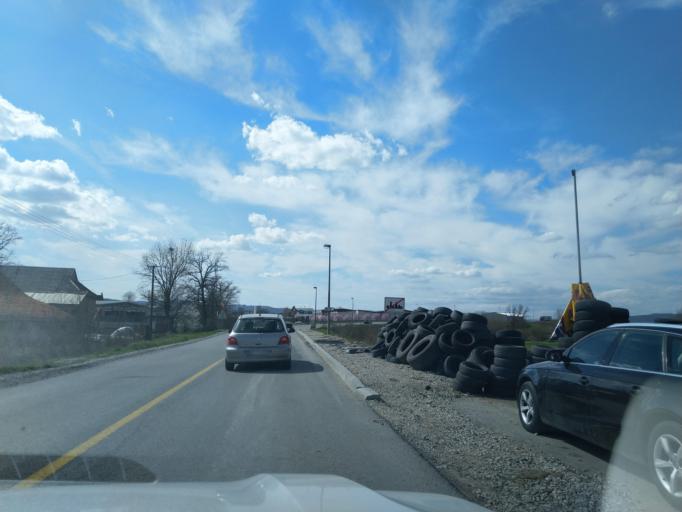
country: RS
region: Central Serbia
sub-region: Zlatiborski Okrug
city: Pozega
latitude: 43.8318
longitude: 20.0488
